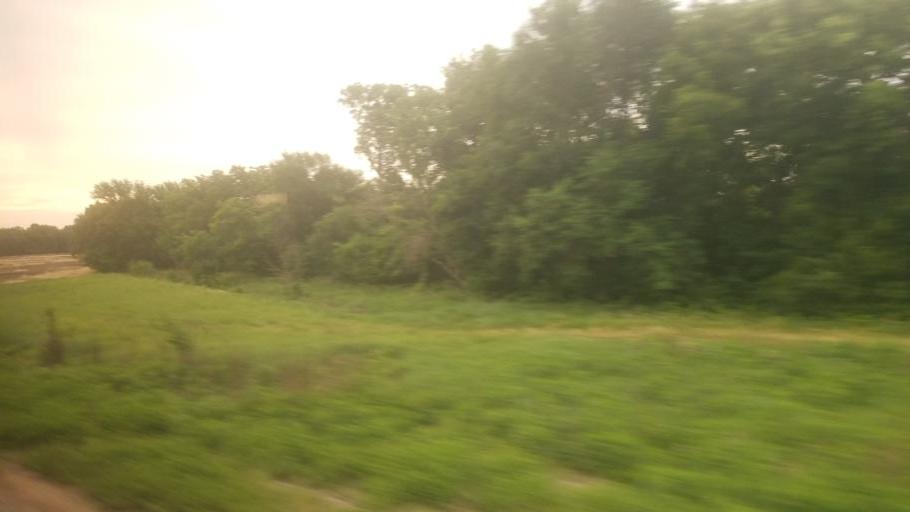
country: US
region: Kansas
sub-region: Chase County
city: Cottonwood Falls
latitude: 38.3961
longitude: -96.5888
